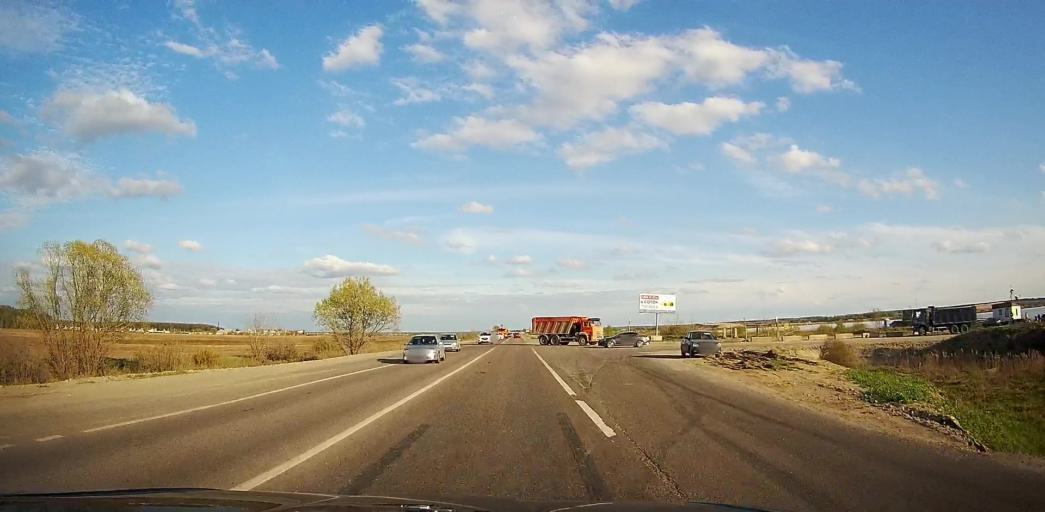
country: RU
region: Moskovskaya
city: Ramenskoye
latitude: 55.5123
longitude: 38.2793
